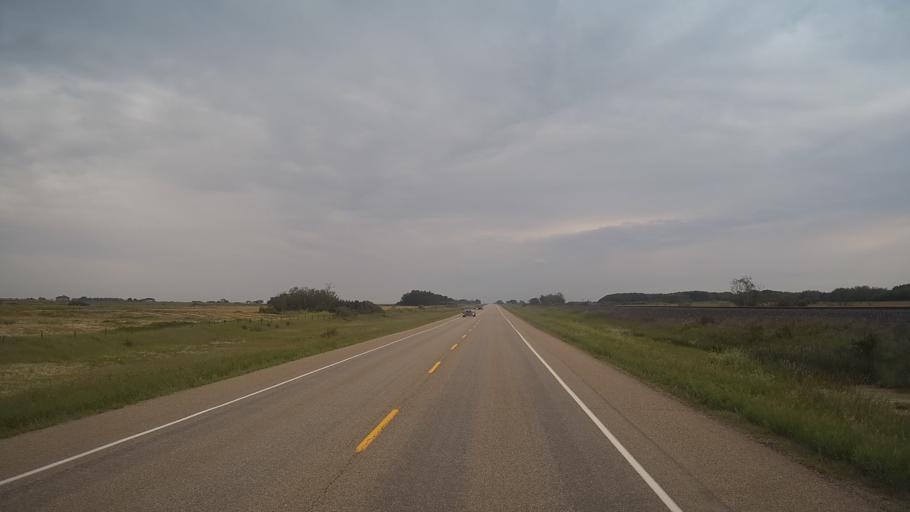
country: CA
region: Saskatchewan
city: Langham
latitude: 52.1270
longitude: -107.2674
